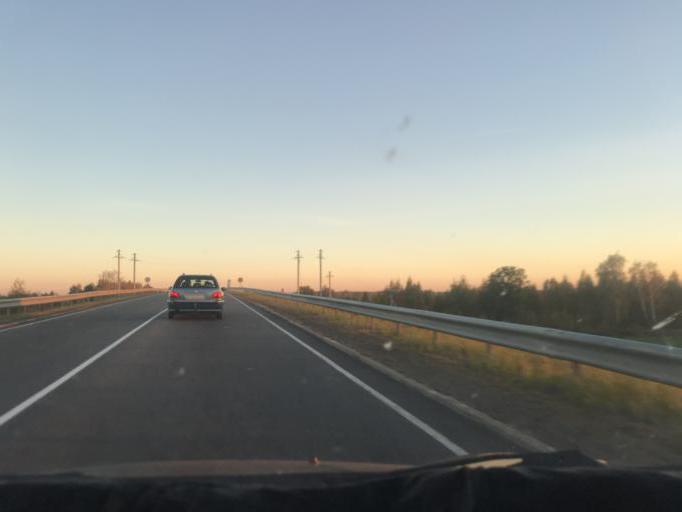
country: BY
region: Gomel
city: Kalinkavichy
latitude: 52.1384
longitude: 29.2570
